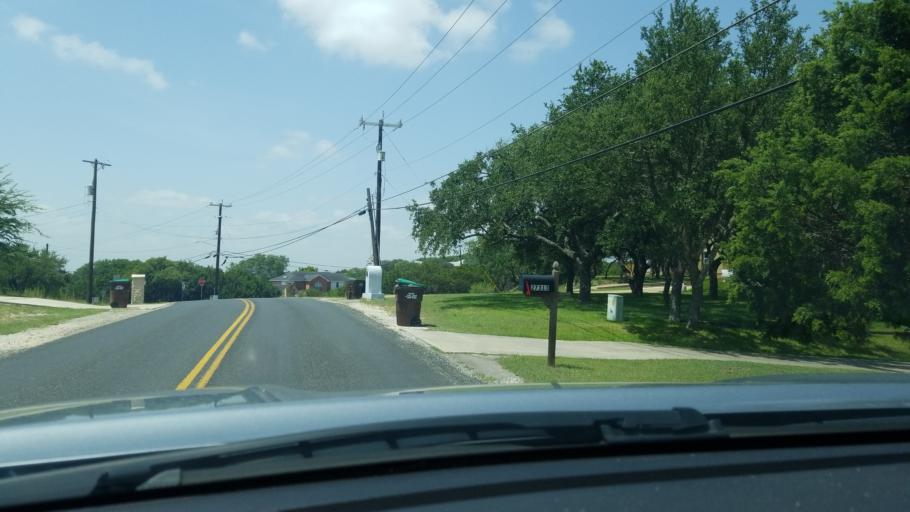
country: US
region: Texas
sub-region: Bexar County
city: Timberwood Park
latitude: 29.7050
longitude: -98.4904
